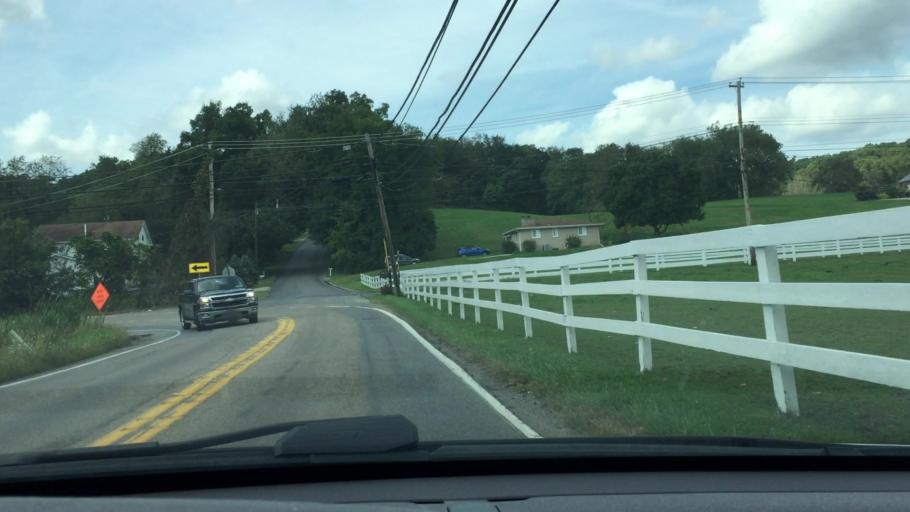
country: US
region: Pennsylvania
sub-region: Washington County
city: Thompsonville
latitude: 40.3074
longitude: -80.1363
